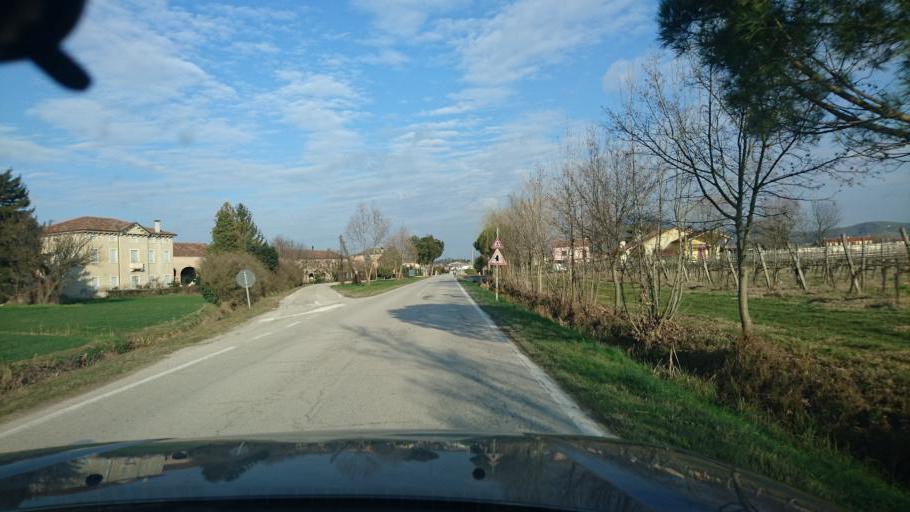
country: IT
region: Veneto
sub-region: Provincia di Vicenza
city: Albettone
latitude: 45.3571
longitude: 11.5720
